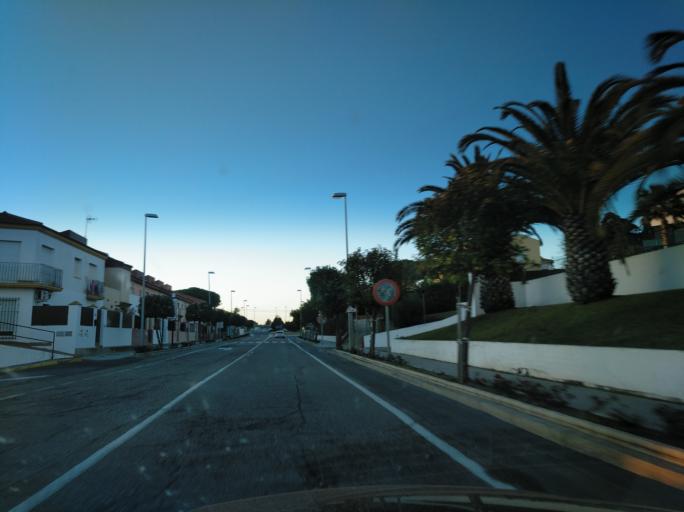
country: ES
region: Andalusia
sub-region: Provincia de Huelva
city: Ayamonte
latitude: 37.2246
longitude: -7.4026
